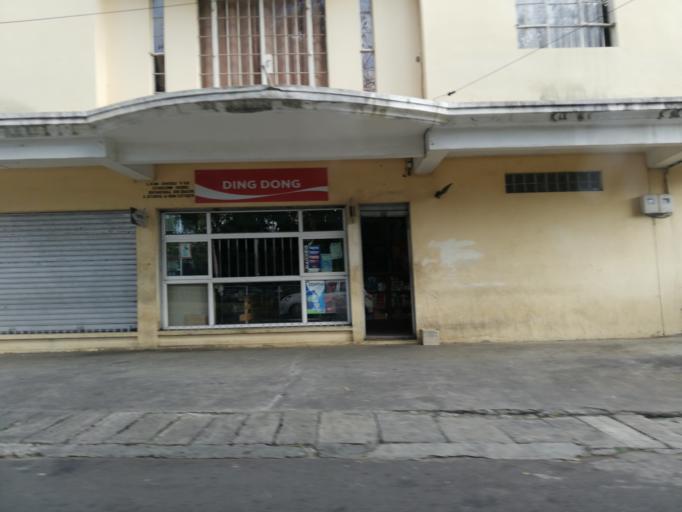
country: MU
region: Plaines Wilhems
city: Ebene
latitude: -20.2307
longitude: 57.4624
